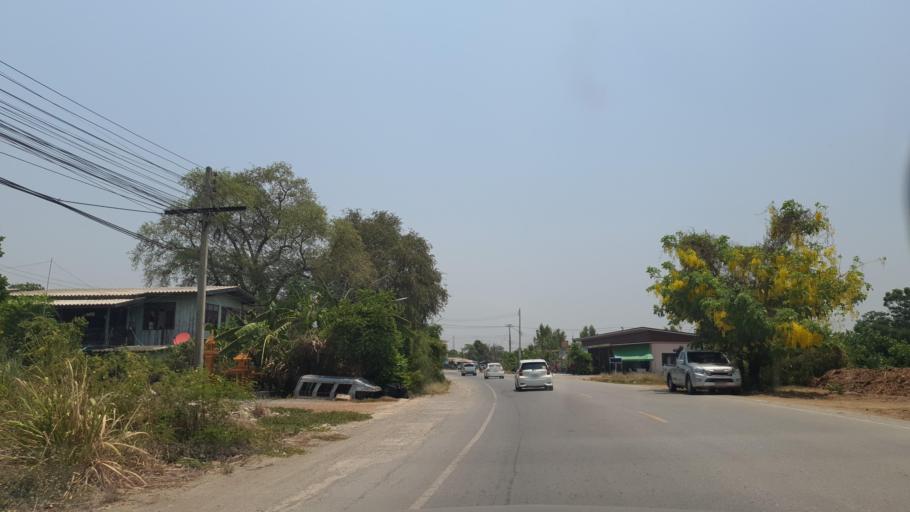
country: TH
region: Suphan Buri
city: Si Prachan
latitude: 14.6725
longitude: 100.1095
